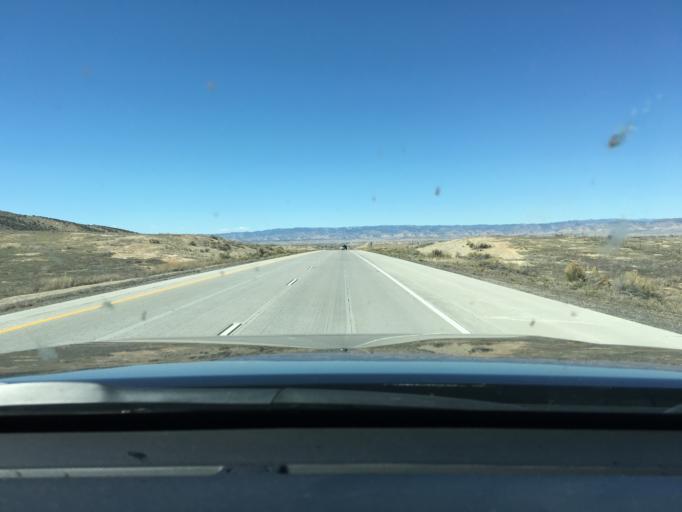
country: US
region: Colorado
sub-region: Mesa County
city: Loma
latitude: 39.2040
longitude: -108.8547
